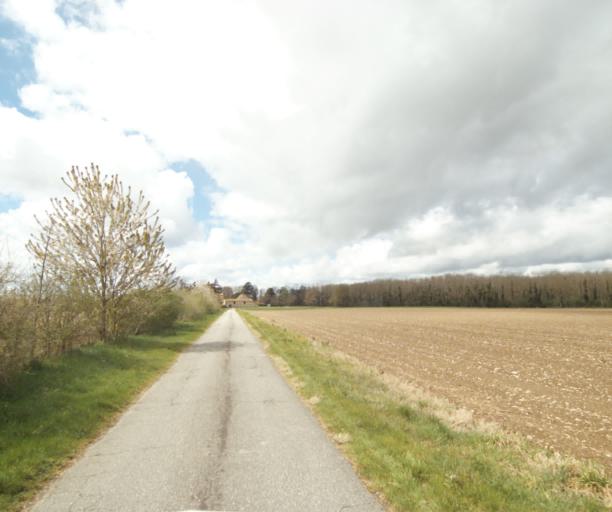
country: FR
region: Midi-Pyrenees
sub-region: Departement de la Haute-Garonne
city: Calmont
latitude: 43.2546
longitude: 1.6292
